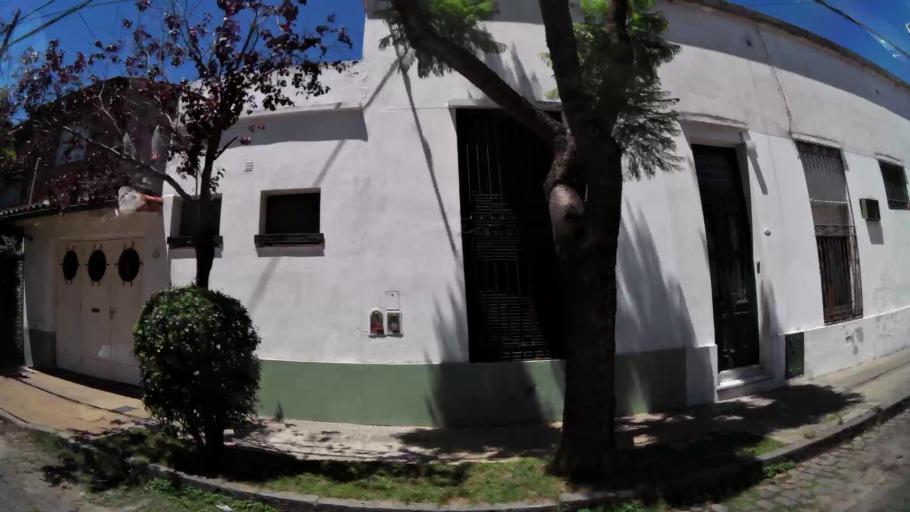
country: AR
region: Buenos Aires
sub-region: Partido de Tigre
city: Tigre
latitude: -34.4448
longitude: -58.5562
